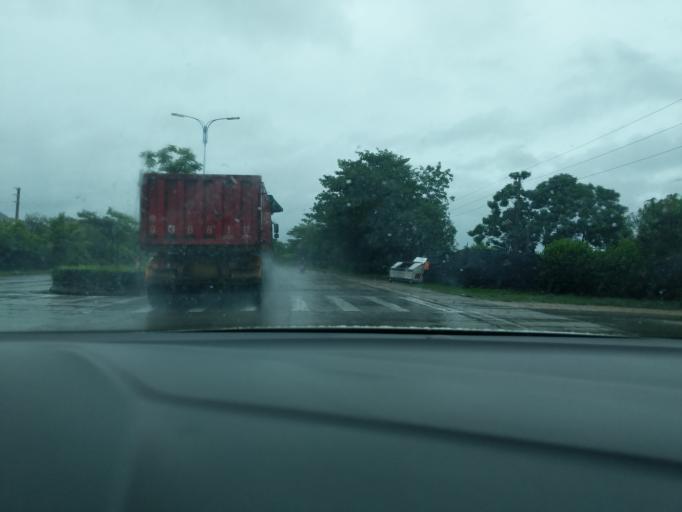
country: CN
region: Guangdong
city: Pingshi
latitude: 22.2095
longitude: 112.3248
